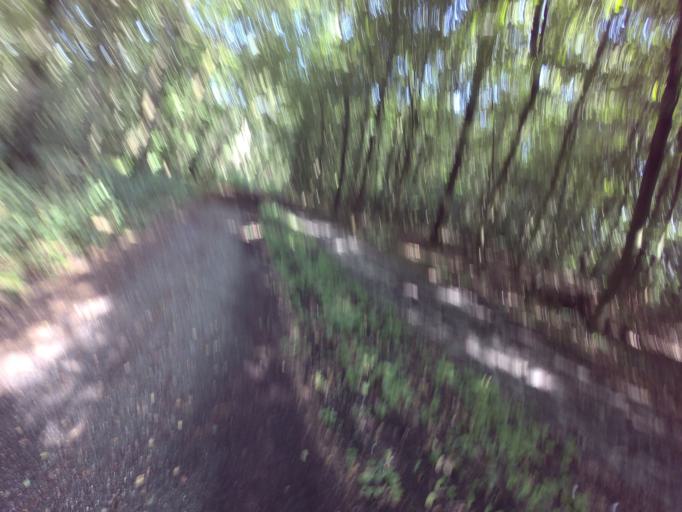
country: BE
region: Wallonia
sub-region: Province de Liege
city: Plombieres
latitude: 50.7568
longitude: 5.9811
